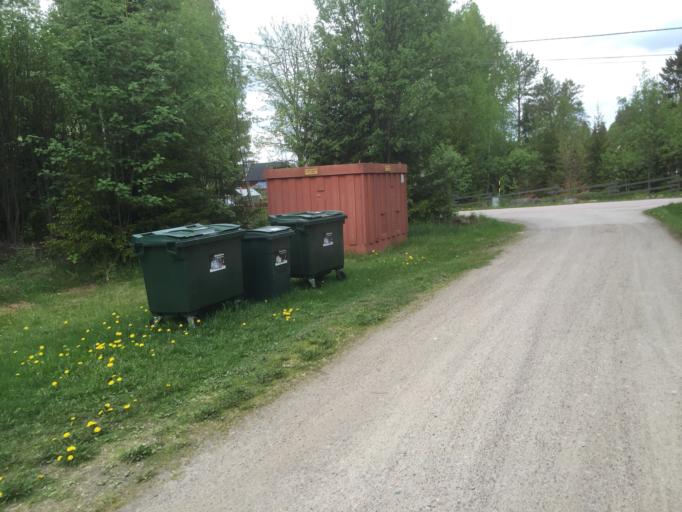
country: SE
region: Uppsala
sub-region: Alvkarleby Kommun
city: Skutskaer
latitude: 60.7917
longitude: 17.2968
